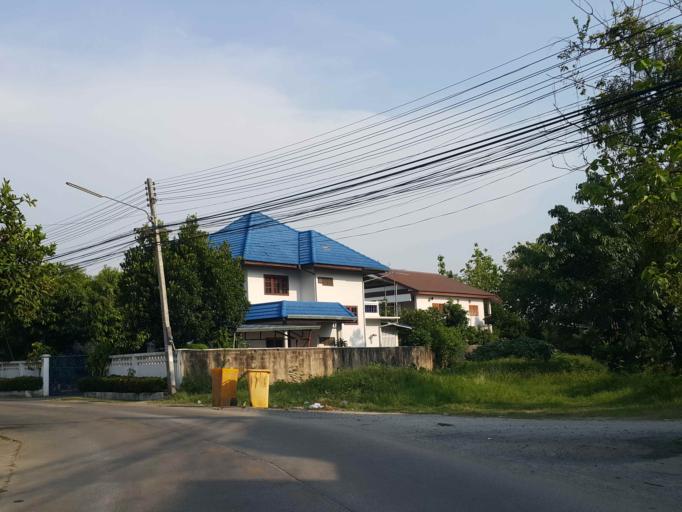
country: TH
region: Chiang Mai
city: Chiang Mai
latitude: 18.7657
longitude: 99.0262
